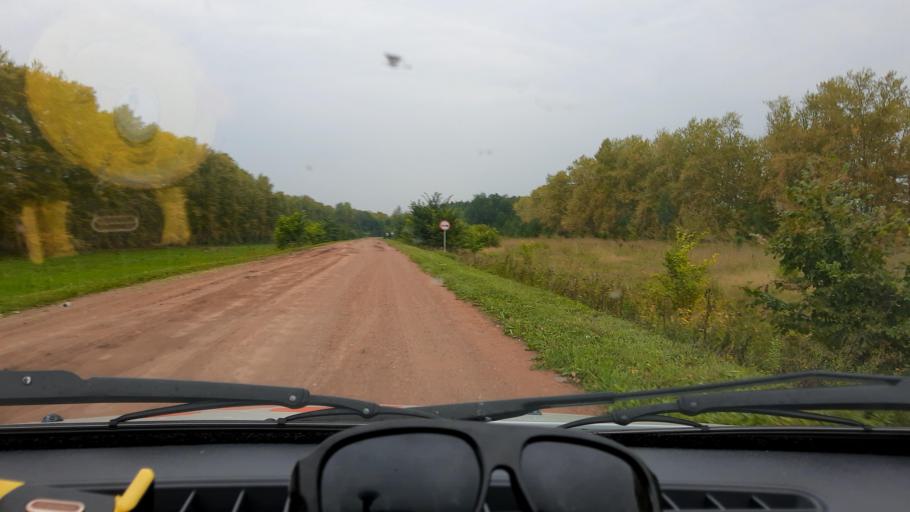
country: RU
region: Bashkortostan
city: Asanovo
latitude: 54.9913
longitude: 55.6959
